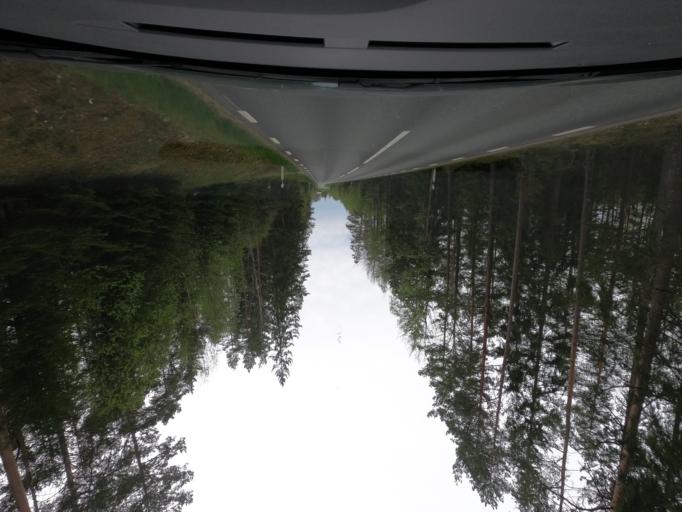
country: SE
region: Joenkoeping
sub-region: Varnamo Kommun
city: Bredaryd
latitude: 57.1951
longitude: 13.7618
